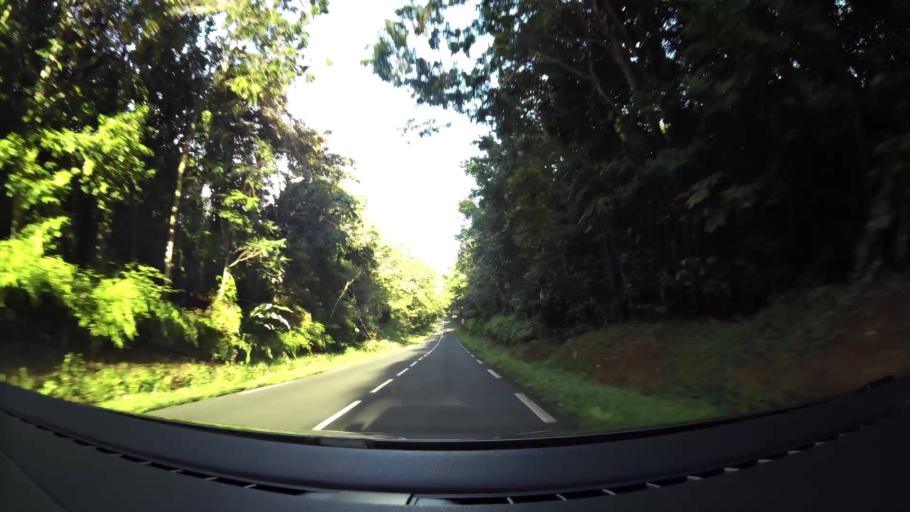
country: GP
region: Guadeloupe
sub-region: Guadeloupe
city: Petit-Bourg
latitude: 16.1812
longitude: -61.6844
